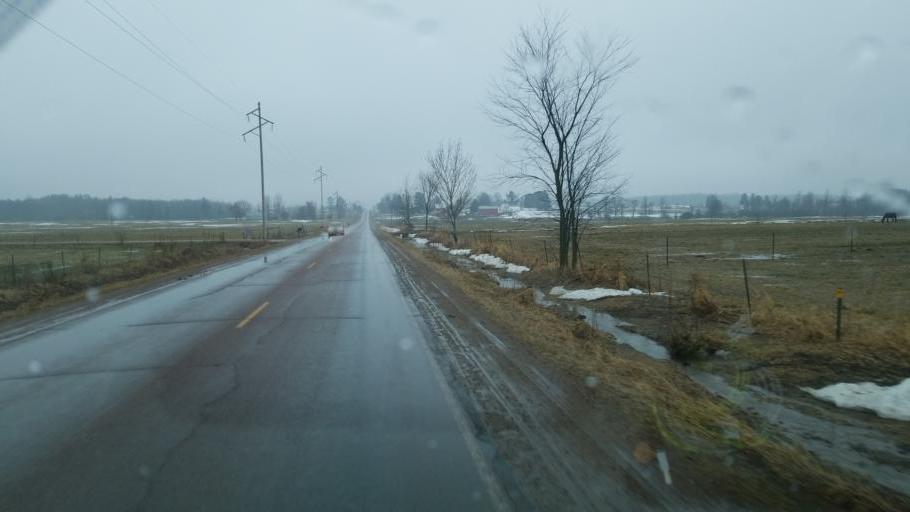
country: US
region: Wisconsin
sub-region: Clark County
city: Loyal
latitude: 44.5754
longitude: -90.3958
